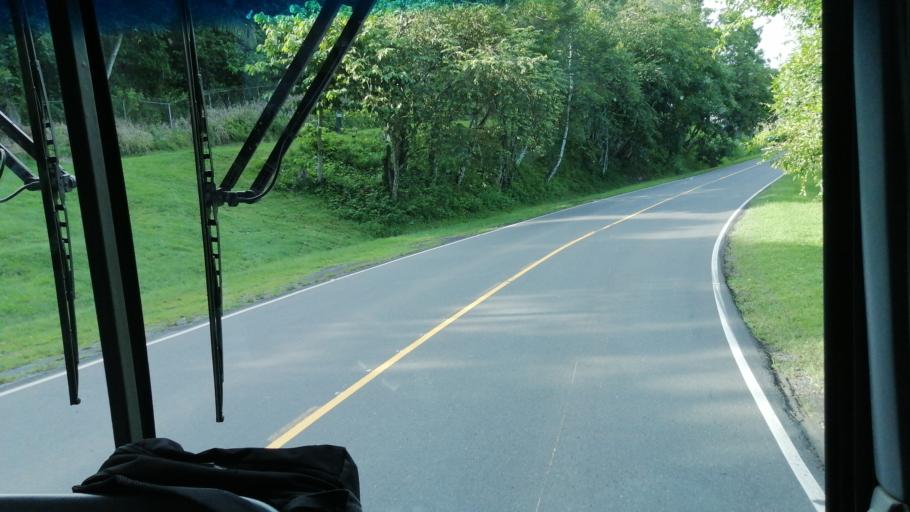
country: PA
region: Panama
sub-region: Distrito de Panama
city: Ancon
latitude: 8.9420
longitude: -79.5915
